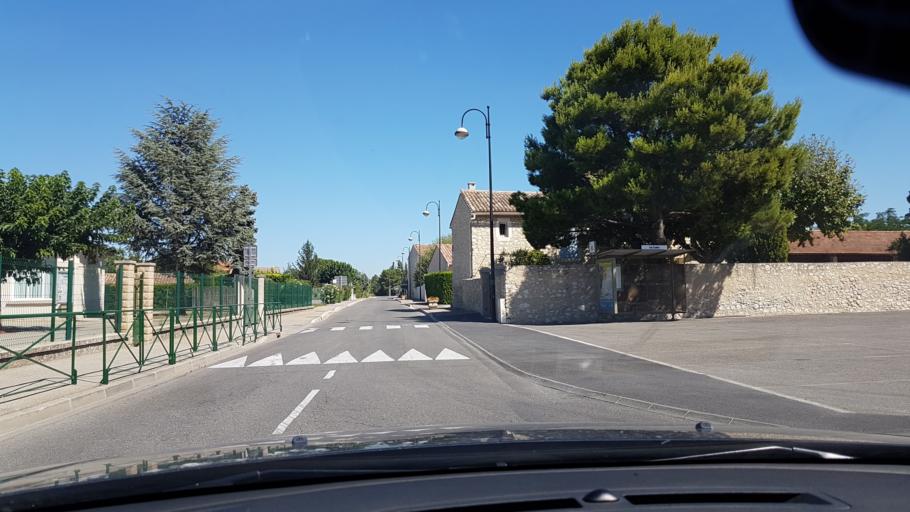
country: FR
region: Provence-Alpes-Cote d'Azur
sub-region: Departement des Bouches-du-Rhone
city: Molleges
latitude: 43.8080
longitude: 4.9490
